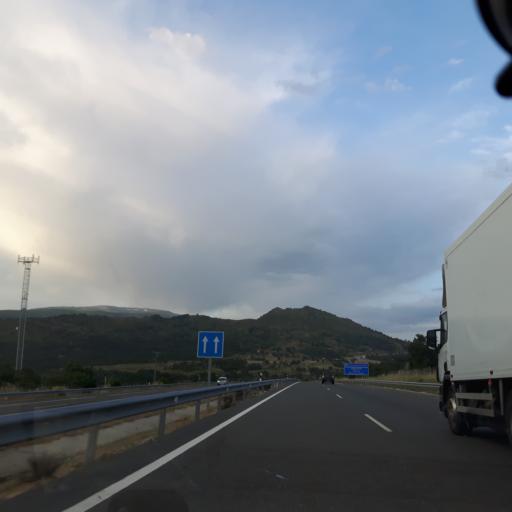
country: ES
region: Castille and Leon
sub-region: Provincia de Salamanca
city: Sorihuela
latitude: 40.4470
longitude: -5.6852
